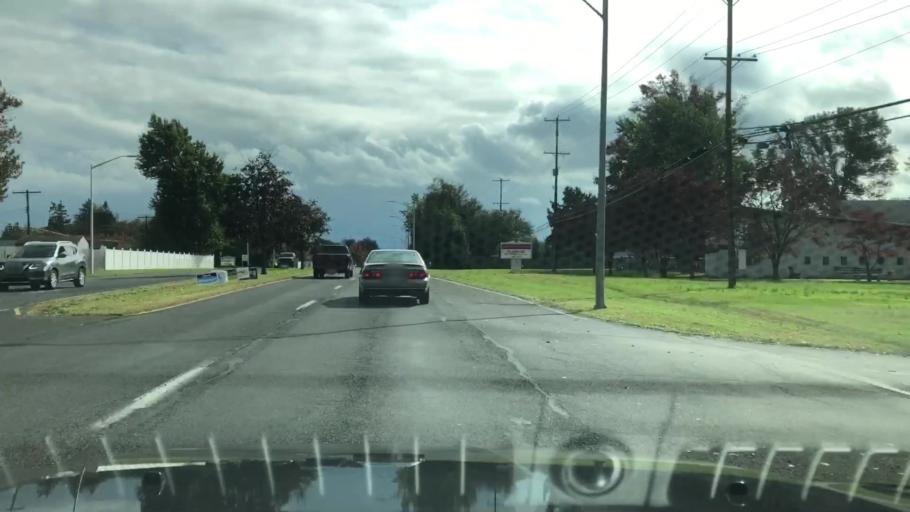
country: US
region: Pennsylvania
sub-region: Bucks County
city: Levittown
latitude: 40.1516
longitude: -74.8259
